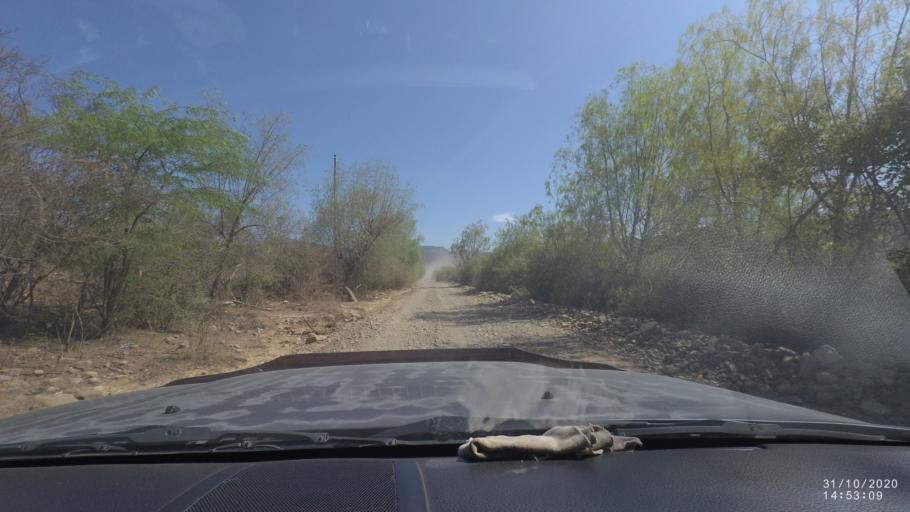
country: BO
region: Cochabamba
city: Aiquile
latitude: -18.2170
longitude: -64.8571
